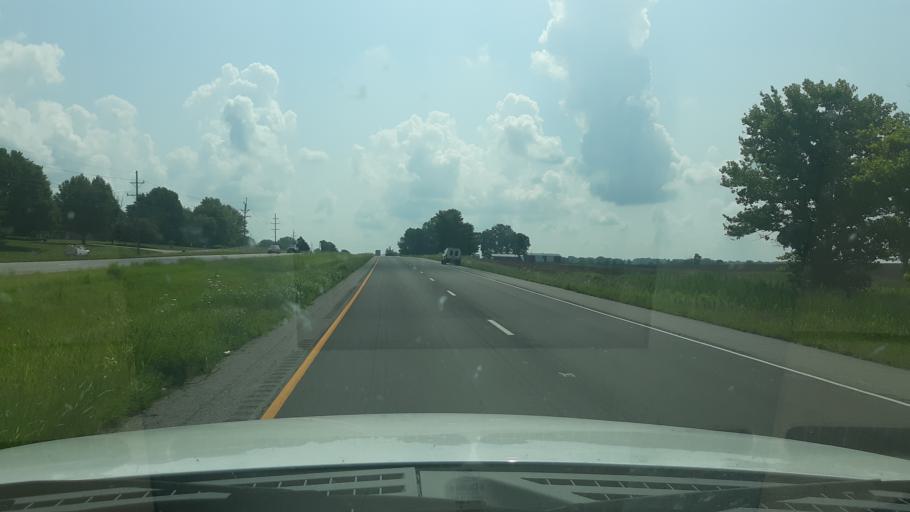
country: US
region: Illinois
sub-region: Williamson County
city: Marion
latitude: 37.7293
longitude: -88.8691
